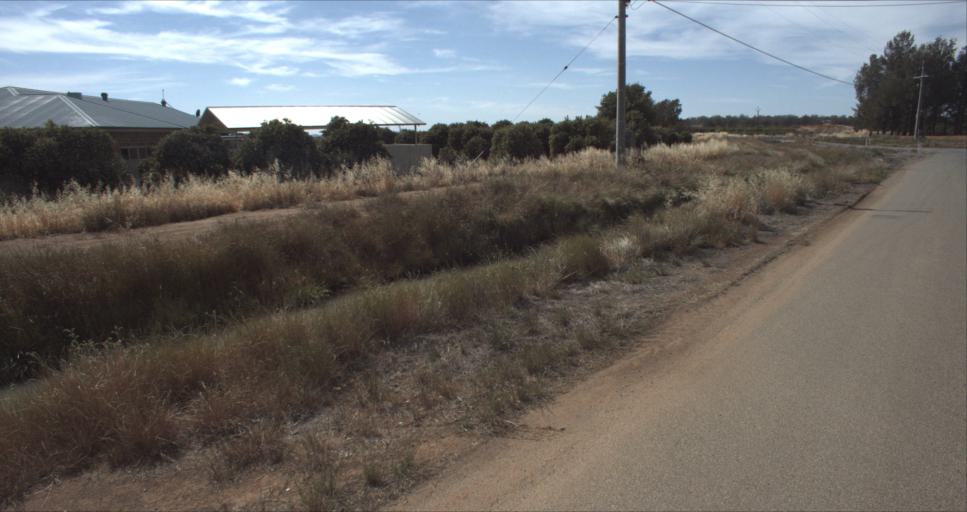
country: AU
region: New South Wales
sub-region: Leeton
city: Leeton
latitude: -34.5906
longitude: 146.4627
